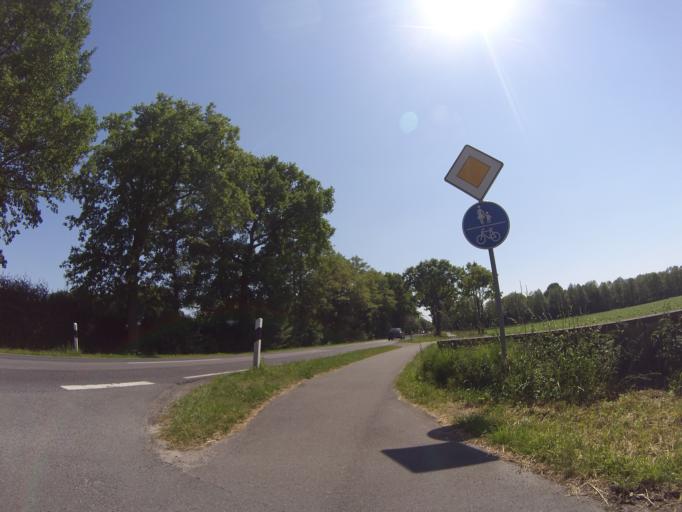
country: DE
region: Lower Saxony
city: Emlichheim
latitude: 52.6222
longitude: 6.8570
